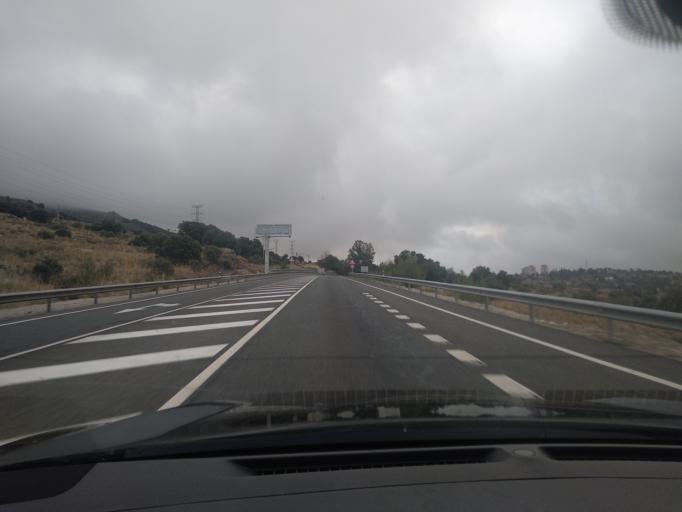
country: ES
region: Castille and Leon
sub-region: Provincia de Segovia
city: Otero de Herreros
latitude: 40.7890
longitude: -4.2141
